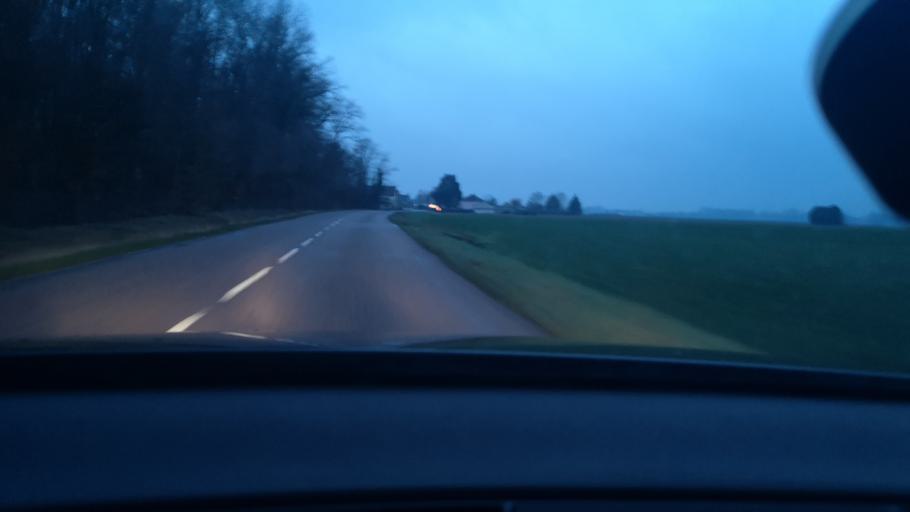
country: FR
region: Bourgogne
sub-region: Departement de Saone-et-Loire
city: Demigny
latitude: 46.9394
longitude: 4.8641
